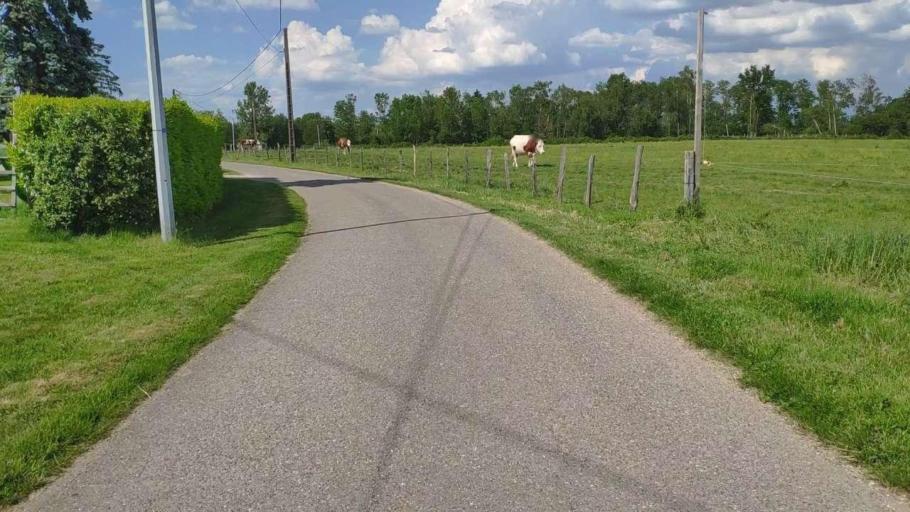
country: FR
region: Franche-Comte
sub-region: Departement du Jura
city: Bletterans
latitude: 46.8148
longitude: 5.3930
